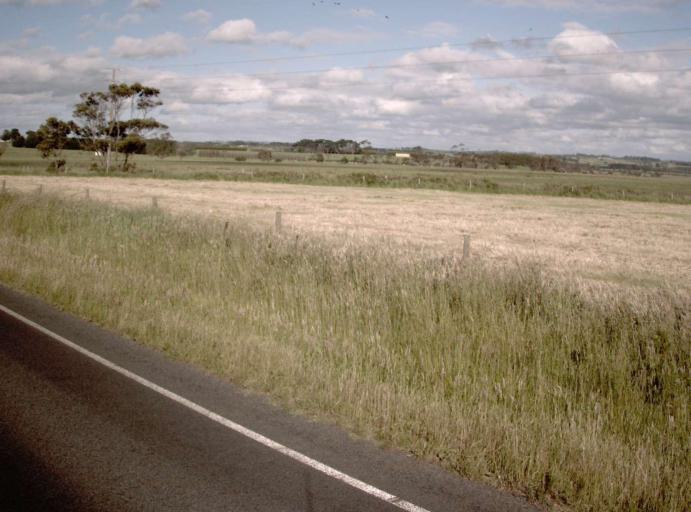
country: AU
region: Victoria
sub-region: Bass Coast
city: North Wonthaggi
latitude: -38.5043
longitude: 145.9137
